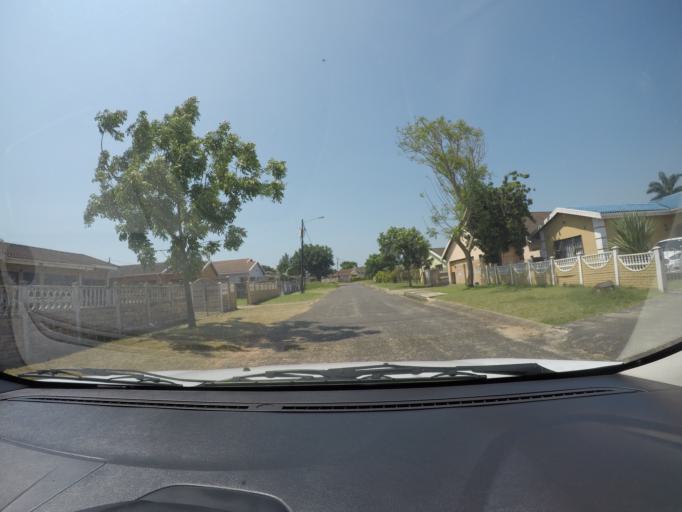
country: ZA
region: KwaZulu-Natal
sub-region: uThungulu District Municipality
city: eSikhawini
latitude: -28.8662
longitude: 31.9235
